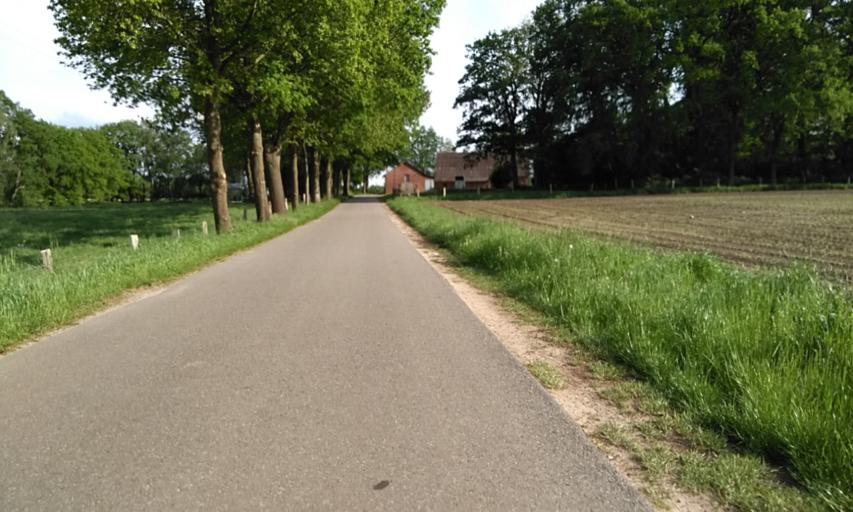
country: DE
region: Lower Saxony
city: Buxtehude
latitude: 53.4585
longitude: 9.7101
